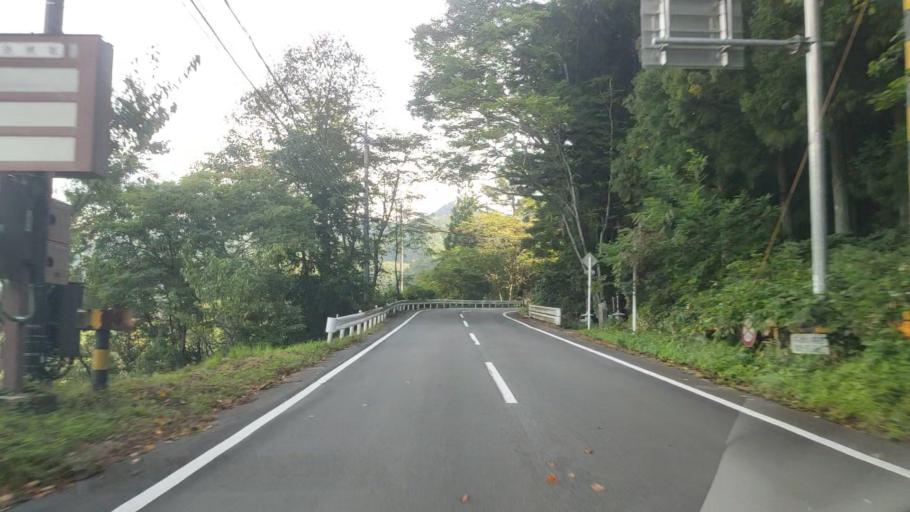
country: JP
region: Gunma
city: Nakanojomachi
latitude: 36.6014
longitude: 138.6350
